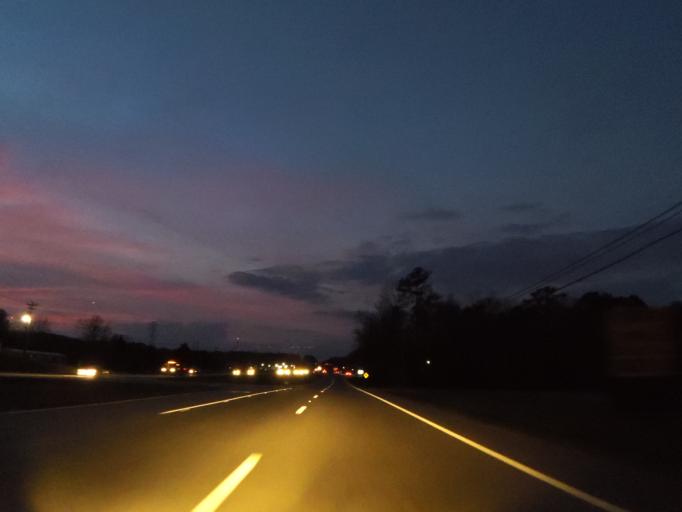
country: US
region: Tennessee
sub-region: Bradley County
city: East Cleveland
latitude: 35.1363
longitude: -84.7707
